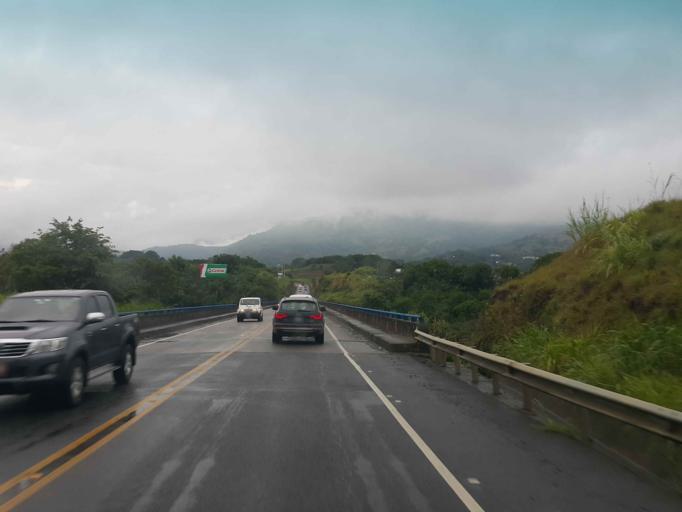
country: CR
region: Heredia
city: Colon
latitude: 9.9484
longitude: -84.2331
